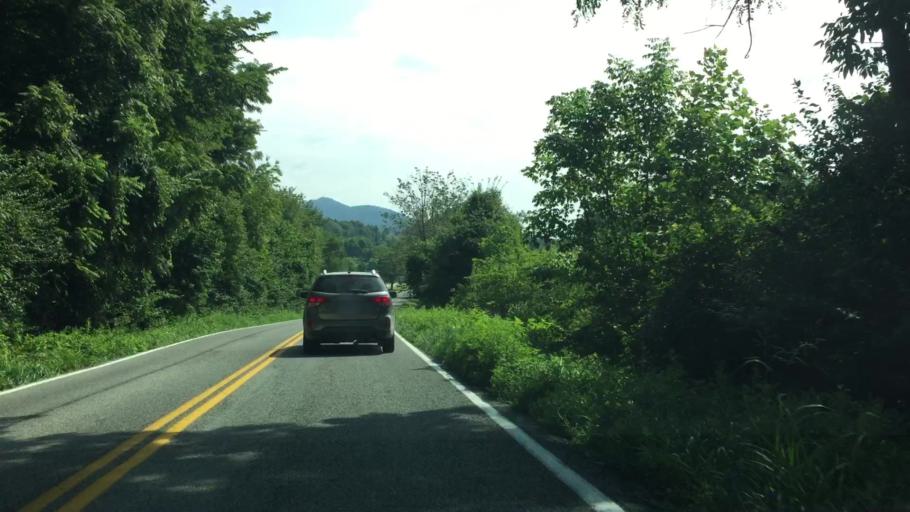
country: US
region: Virginia
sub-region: Pulaski County
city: Pulaski
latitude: 36.9883
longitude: -80.8180
